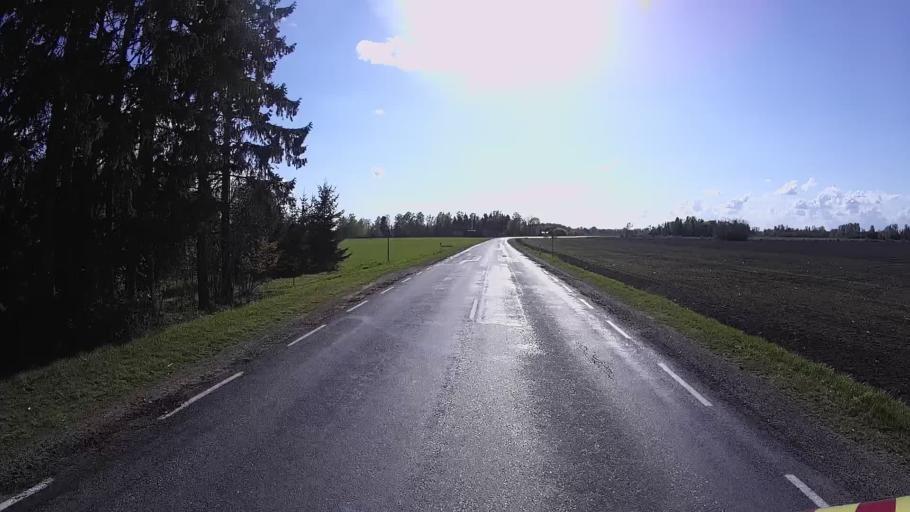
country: EE
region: Viljandimaa
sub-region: Vohma linn
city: Vohma
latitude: 58.6397
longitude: 25.6721
